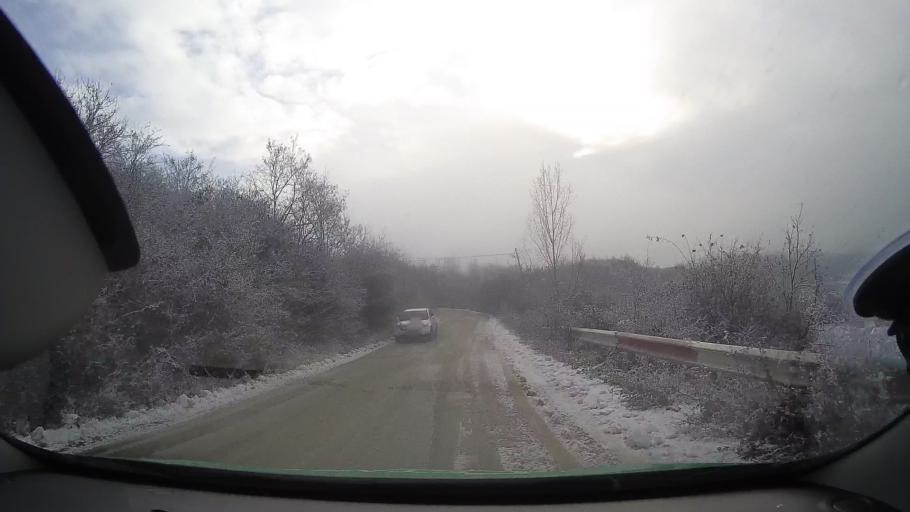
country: RO
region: Mures
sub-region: Comuna Chetani
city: Chetani
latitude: 46.4252
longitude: 24.0113
